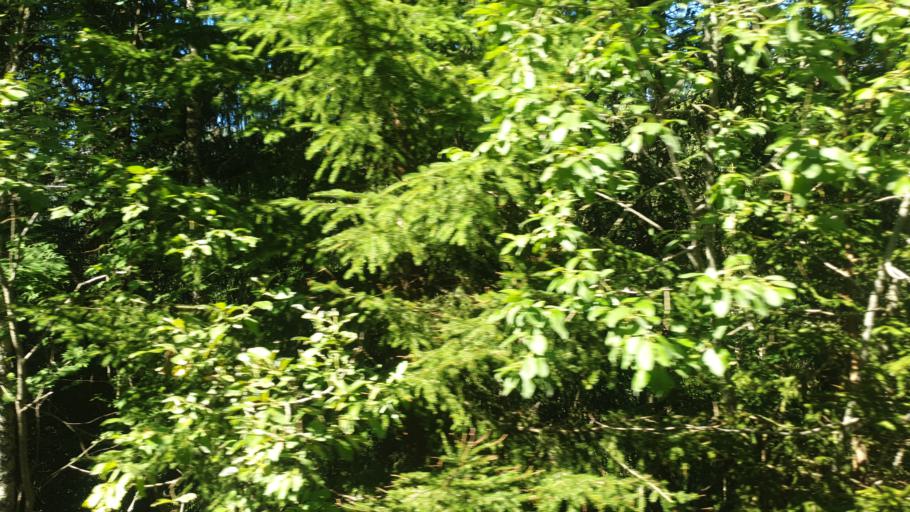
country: NO
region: Sor-Trondelag
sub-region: Meldal
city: Meldal
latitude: 63.1645
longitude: 9.7342
